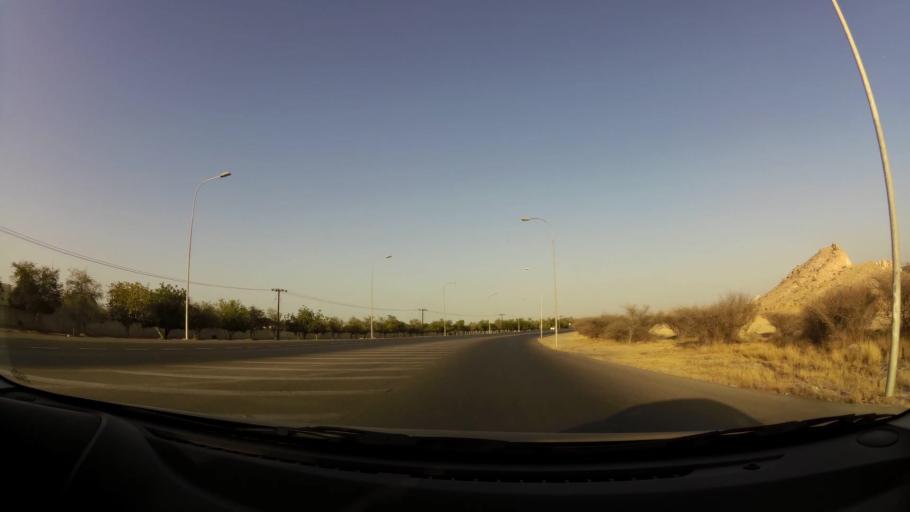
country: OM
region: Muhafazat Masqat
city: As Sib al Jadidah
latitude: 23.5819
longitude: 58.1715
